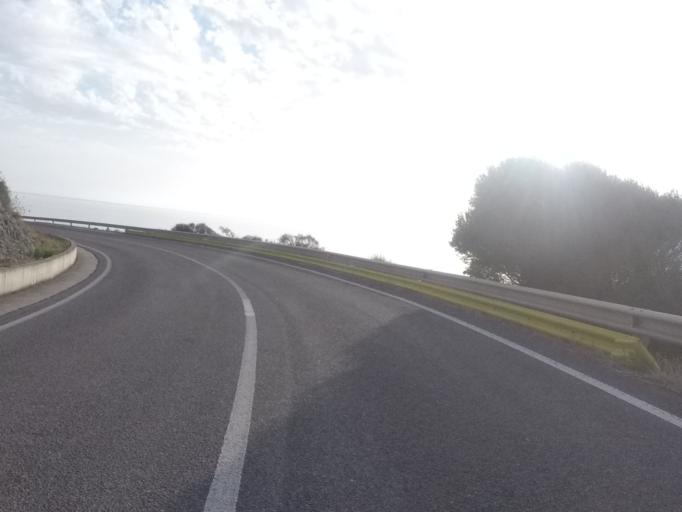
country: IT
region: Sardinia
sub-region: Provincia di Sassari
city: Alghero
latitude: 40.4891
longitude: 8.3763
